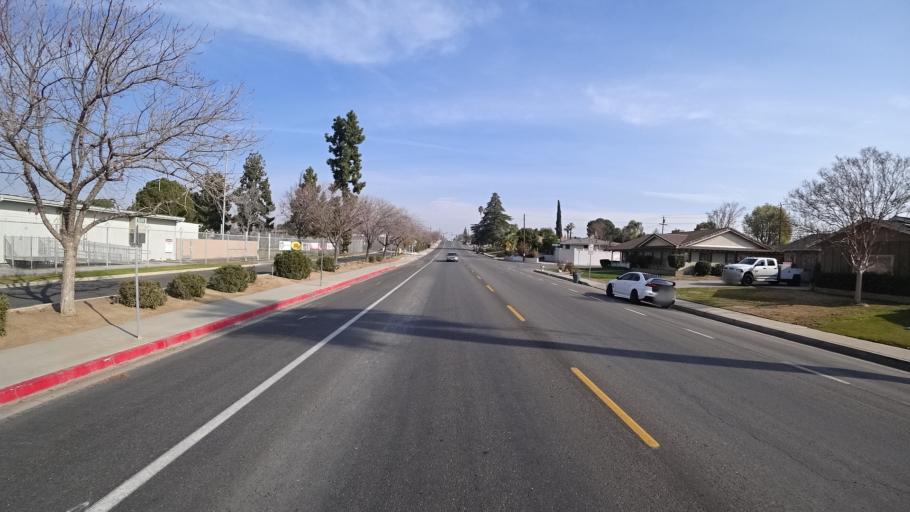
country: US
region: California
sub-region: Kern County
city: Oildale
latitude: 35.4049
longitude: -118.9712
